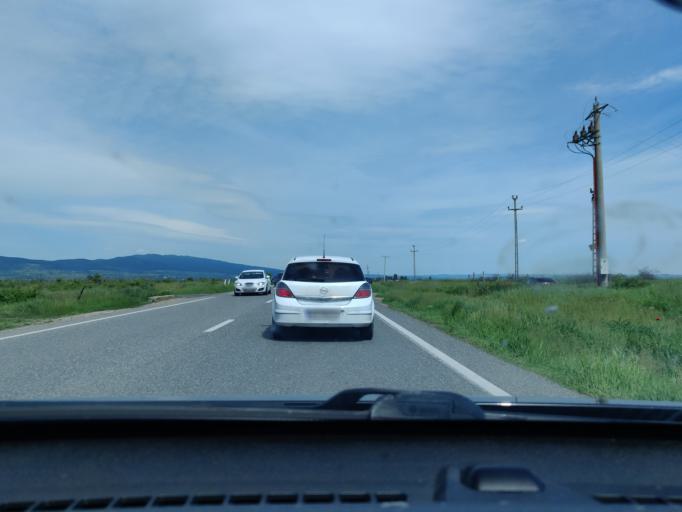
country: RO
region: Vrancea
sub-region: Oras Odobesti
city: Unirea
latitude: 45.7544
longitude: 27.1306
